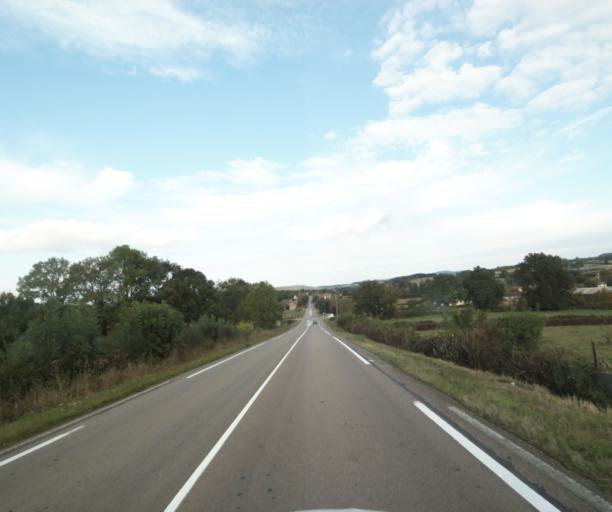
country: FR
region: Bourgogne
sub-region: Departement de Saone-et-Loire
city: Charolles
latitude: 46.4453
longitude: 4.3312
